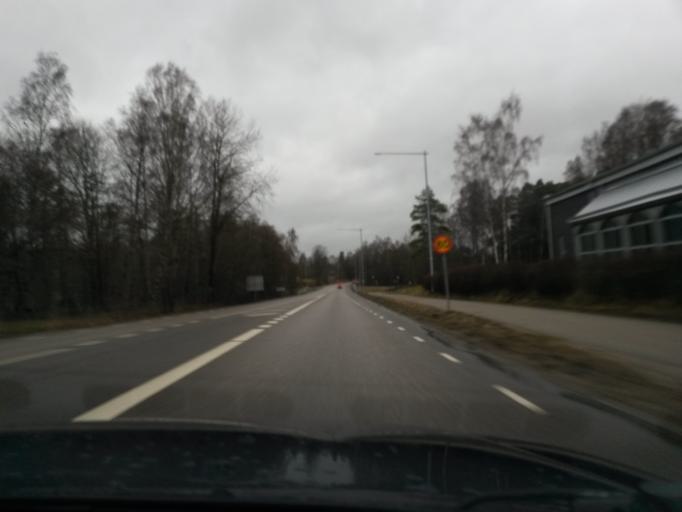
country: SE
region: Vaestra Goetaland
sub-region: Boras Kommun
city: Ganghester
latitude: 57.8047
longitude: 13.0115
